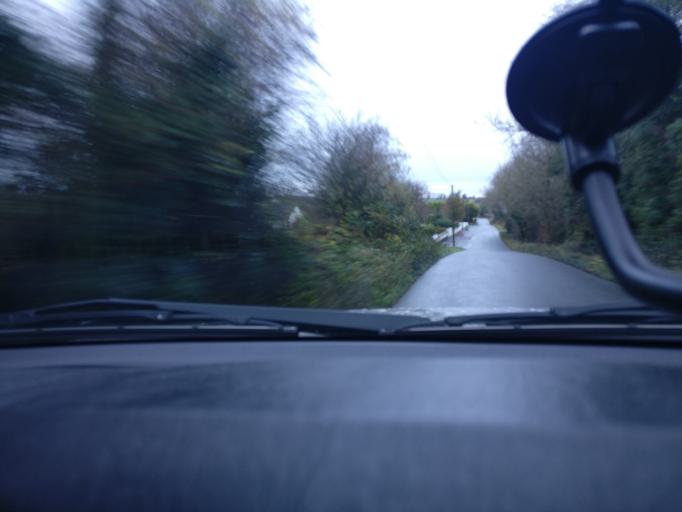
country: IE
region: Connaught
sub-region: County Galway
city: Loughrea
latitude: 53.2545
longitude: -8.5824
